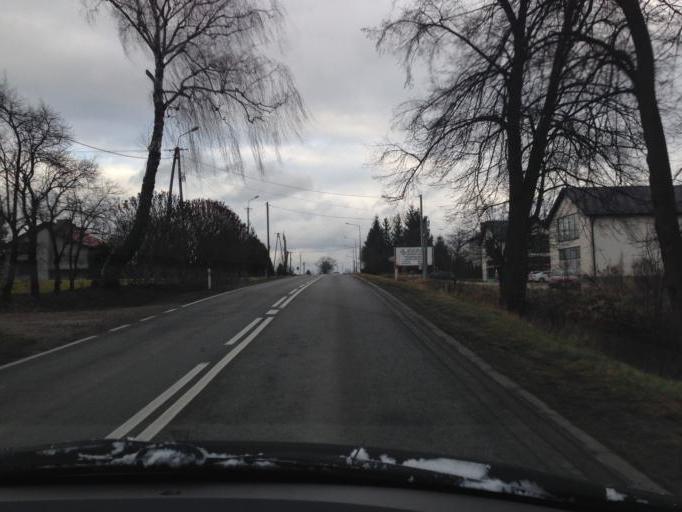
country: PL
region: Lesser Poland Voivodeship
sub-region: Powiat wielicki
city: Gdow
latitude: 49.9075
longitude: 20.1775
